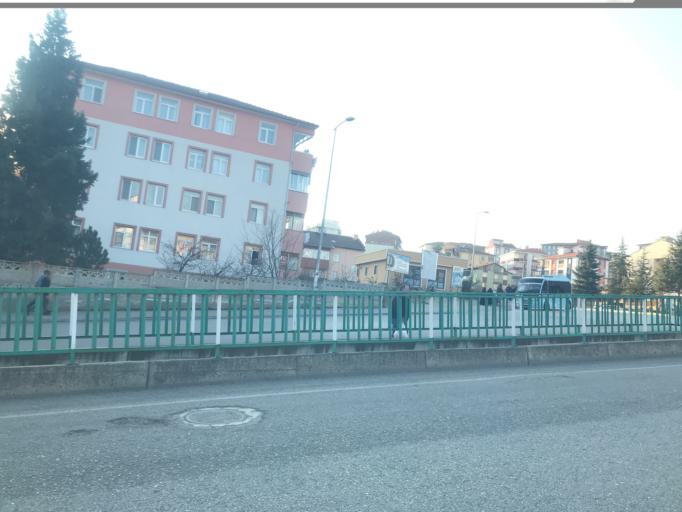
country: TR
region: Karabuk
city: Karabuk
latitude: 41.2179
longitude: 32.6605
